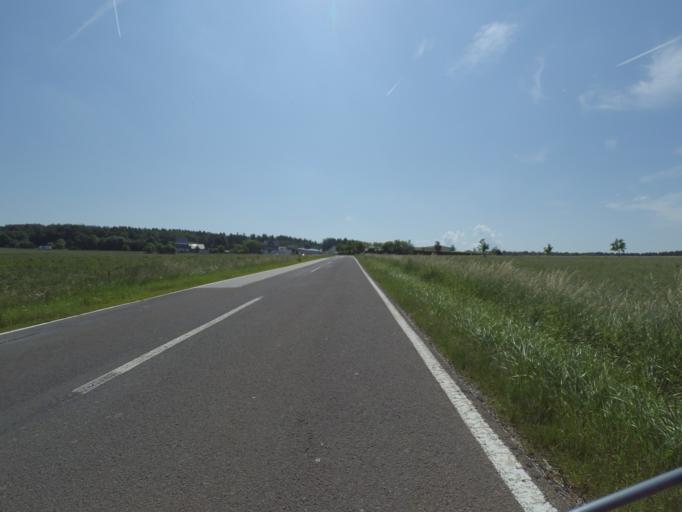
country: DE
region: Rheinland-Pfalz
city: Bell
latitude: 50.0562
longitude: 7.4214
